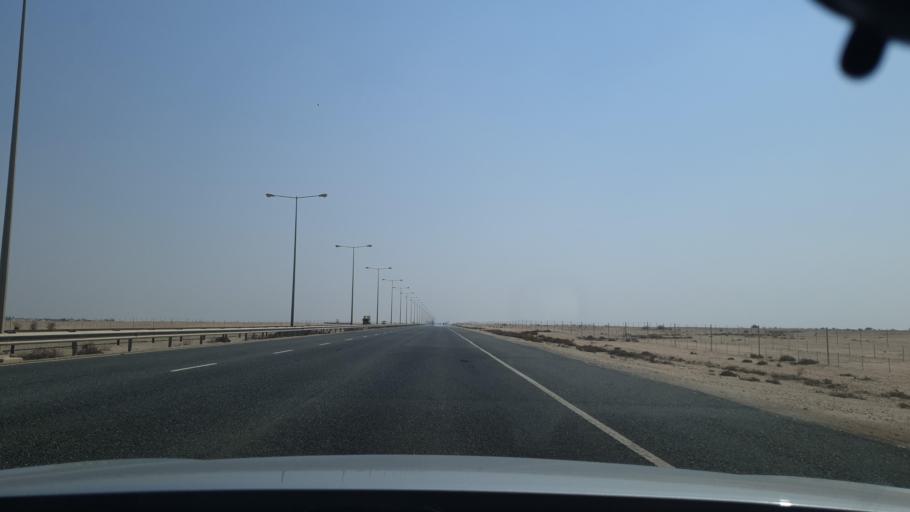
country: QA
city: Al Ghuwayriyah
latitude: 25.8070
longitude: 51.3772
